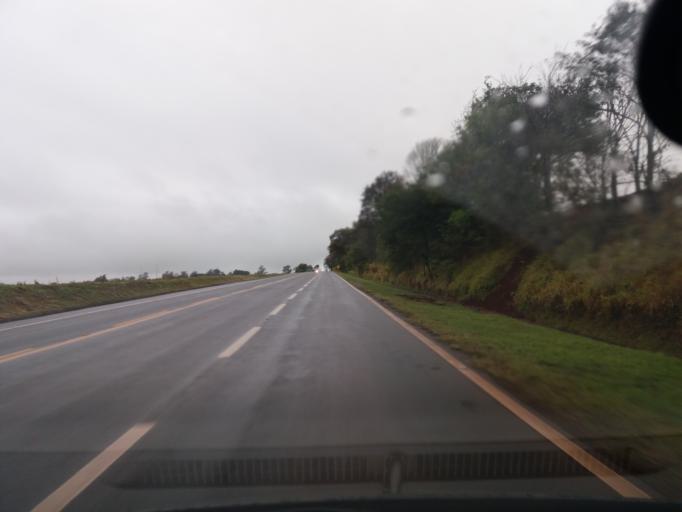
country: BR
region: Parana
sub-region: Campo Mourao
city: Campo Mourao
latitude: -24.3197
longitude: -52.6360
